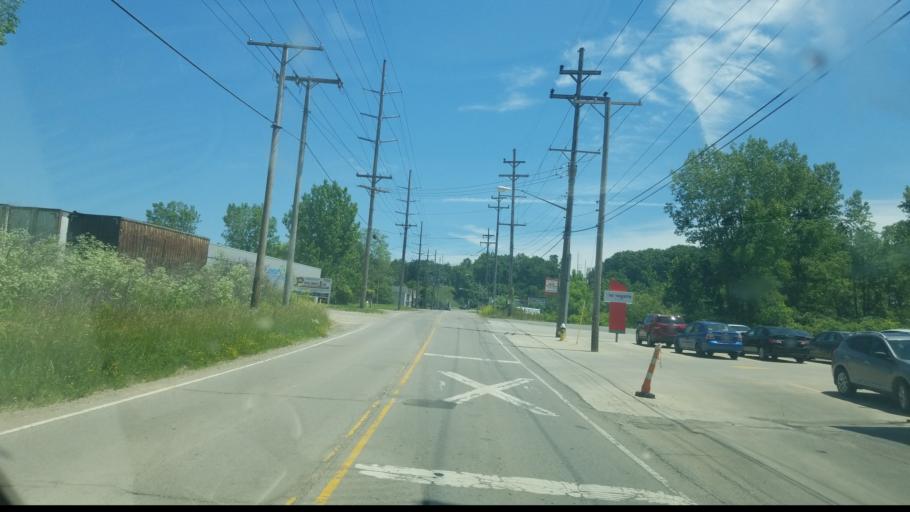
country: US
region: Ohio
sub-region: Richland County
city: Mansfield
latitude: 40.7771
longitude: -82.5089
